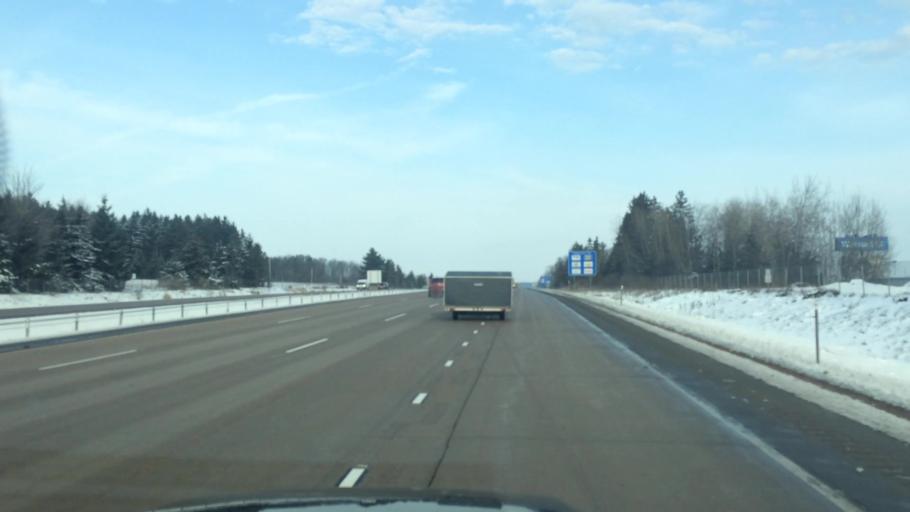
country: US
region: Wisconsin
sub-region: Marathon County
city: Rib Mountain
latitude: 44.9164
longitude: -89.6540
